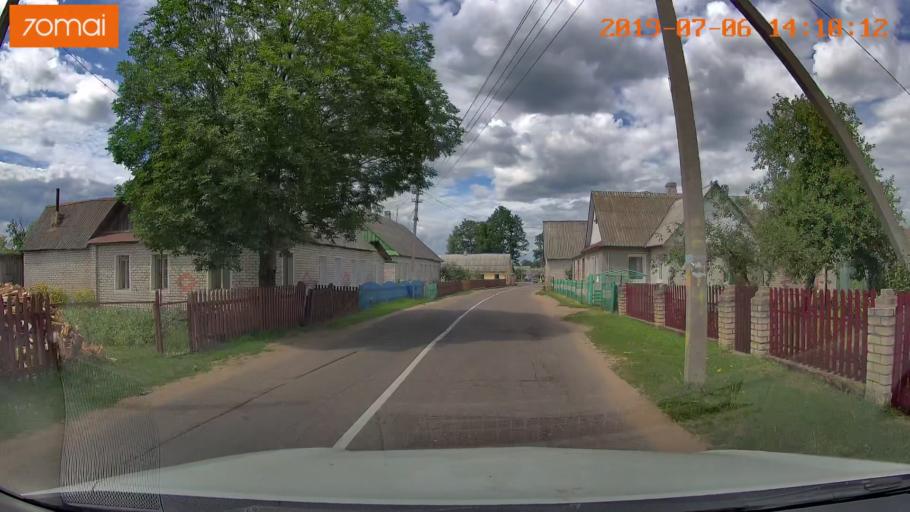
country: BY
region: Minsk
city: Ivyanyets
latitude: 53.8848
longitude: 26.7447
